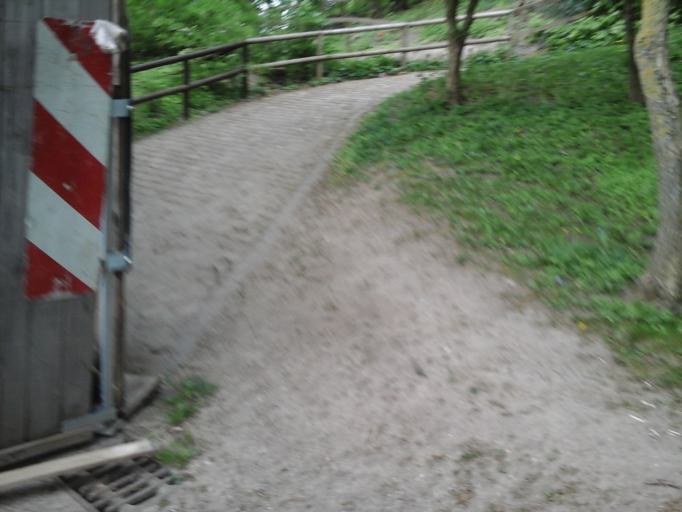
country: DE
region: Baden-Wuerttemberg
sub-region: Karlsruhe Region
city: Heidelberg
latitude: 49.4127
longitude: 8.7182
